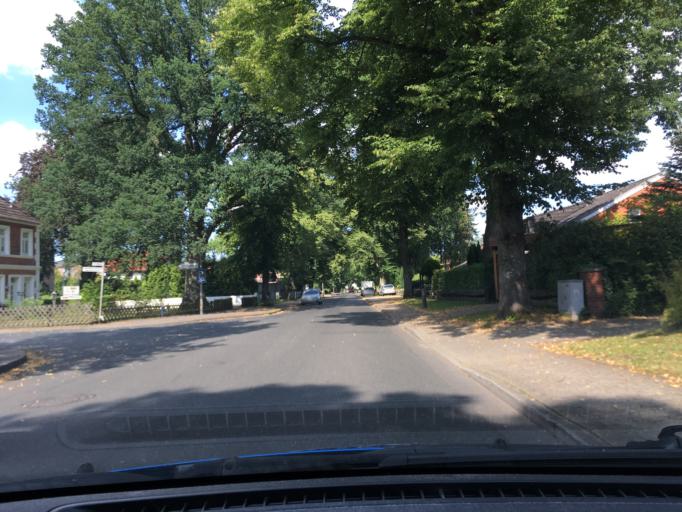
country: DE
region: Lower Saxony
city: Stelle
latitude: 53.3975
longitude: 10.0441
